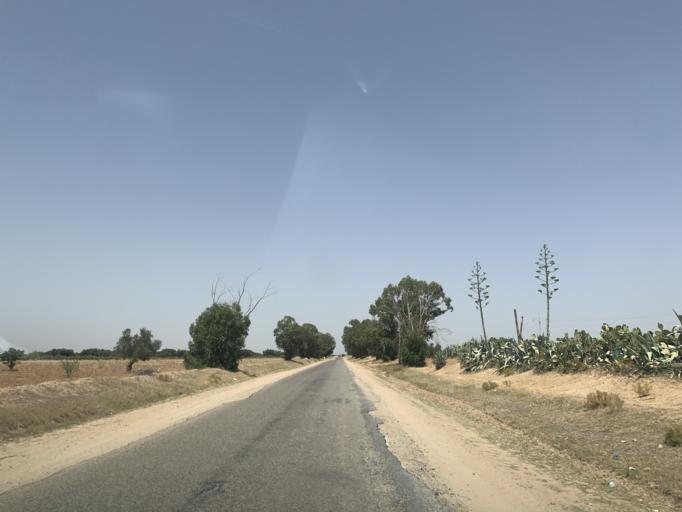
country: TN
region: Al Mahdiyah
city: Shurban
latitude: 35.1751
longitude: 10.2319
